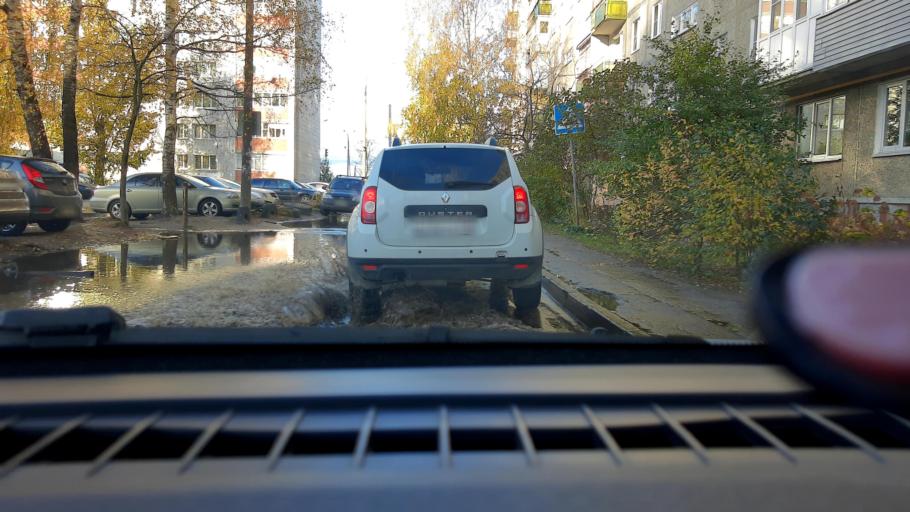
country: RU
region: Nizjnij Novgorod
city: Gorbatovka
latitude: 56.3804
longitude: 43.7978
